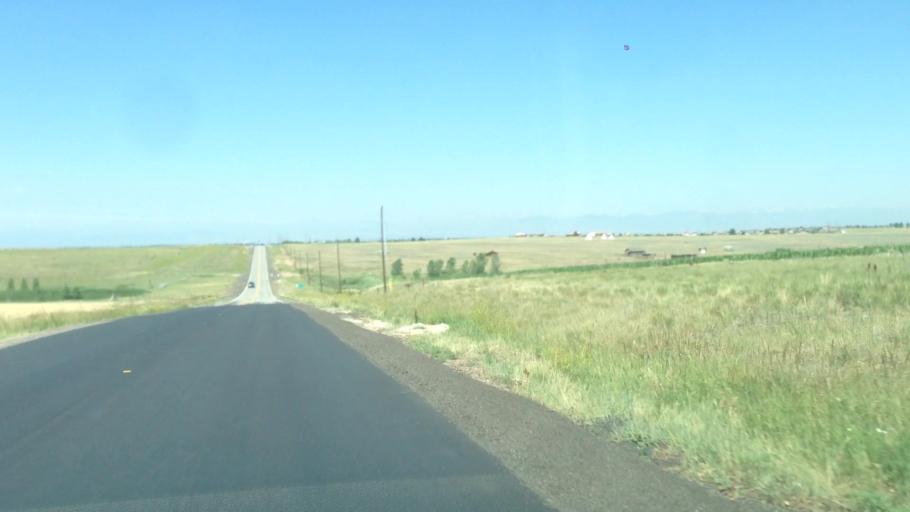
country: US
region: Colorado
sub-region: Arapahoe County
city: Dove Valley
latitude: 39.6530
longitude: -104.7231
